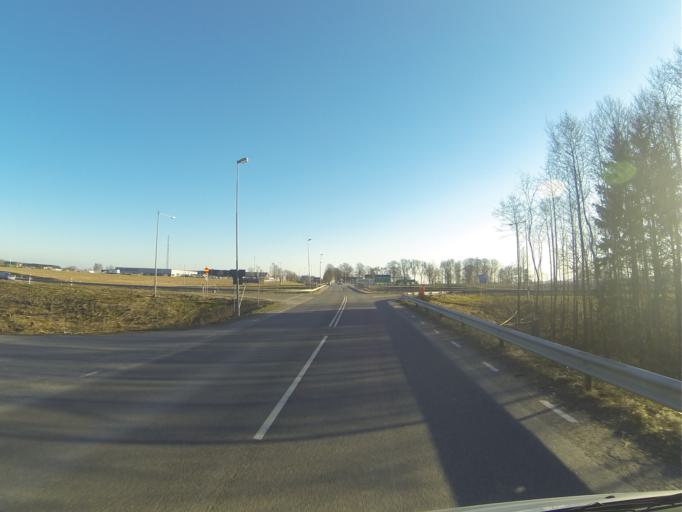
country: SE
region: Skane
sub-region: Horby Kommun
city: Hoerby
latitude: 55.8670
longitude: 13.6626
